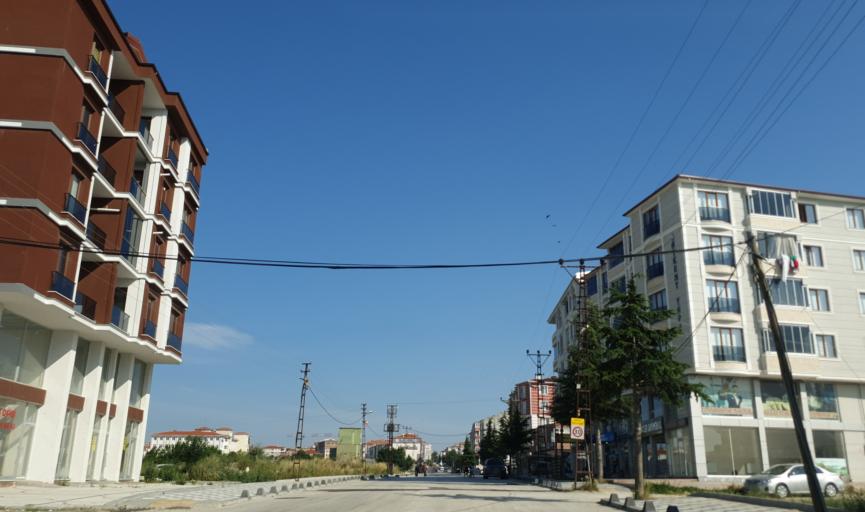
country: TR
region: Tekirdag
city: Saray
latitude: 41.4483
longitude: 27.9141
